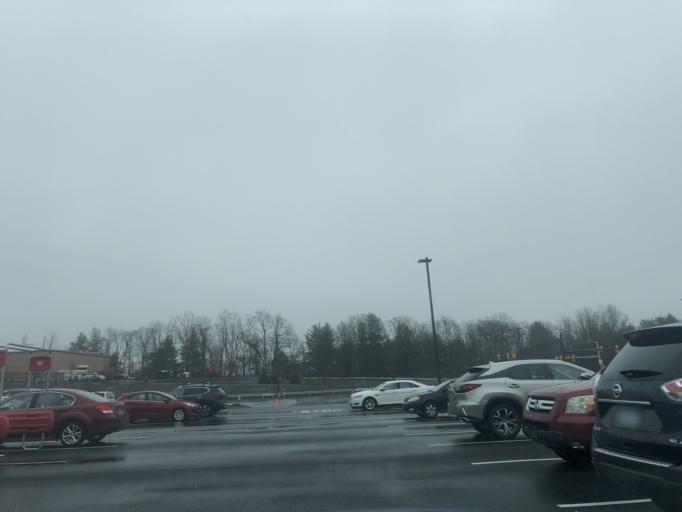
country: US
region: Pennsylvania
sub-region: Delaware County
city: Broomall
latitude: 39.9769
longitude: -75.3441
